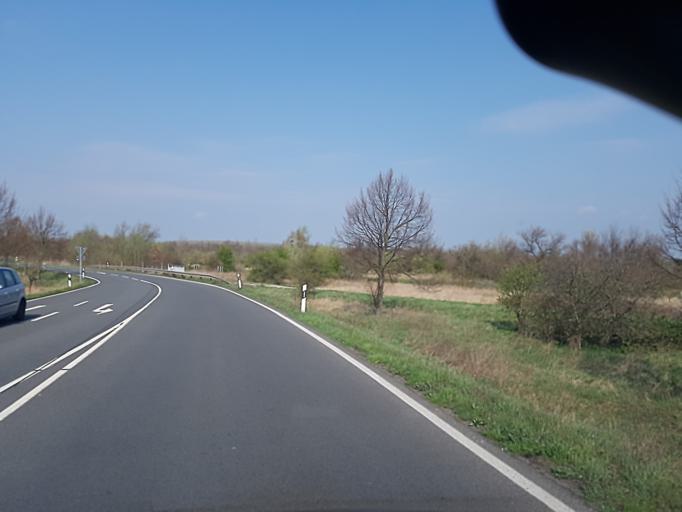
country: DE
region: Saxony-Anhalt
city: Grafenhainichen
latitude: 51.7349
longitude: 12.4403
